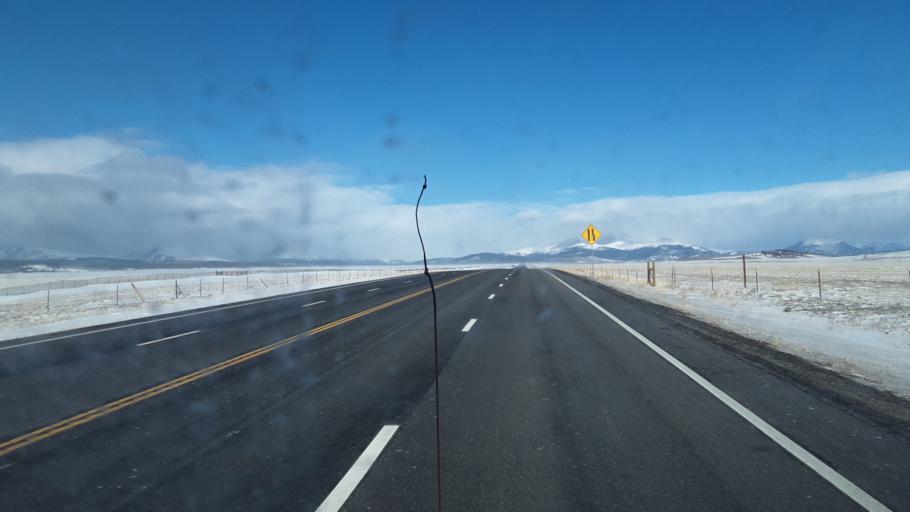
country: US
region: Colorado
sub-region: Park County
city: Fairplay
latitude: 39.1440
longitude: -105.9976
